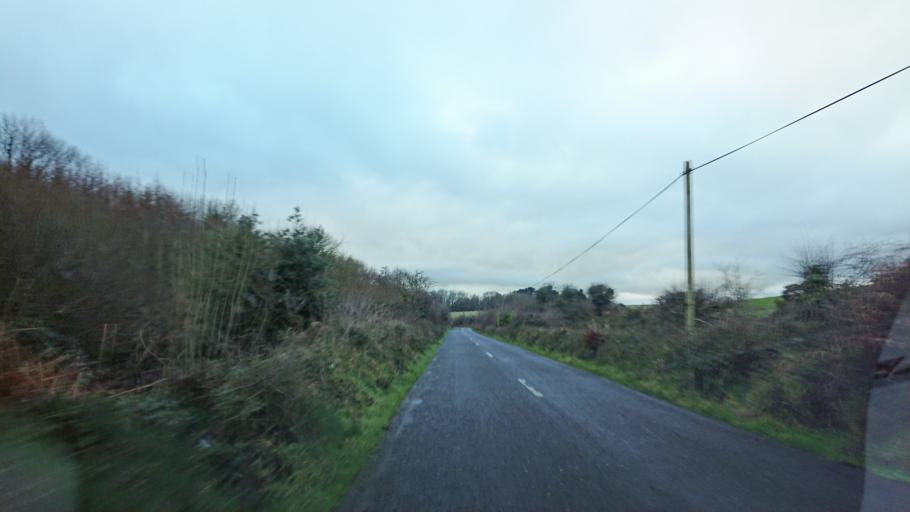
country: IE
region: Munster
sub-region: Waterford
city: Portlaw
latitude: 52.2167
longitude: -7.4174
